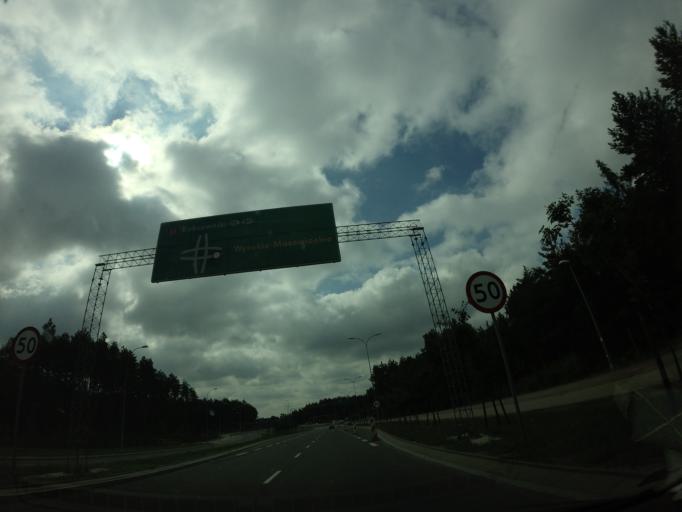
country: PL
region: Podlasie
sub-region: Bialystok
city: Bialystok
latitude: 53.1306
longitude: 23.2222
